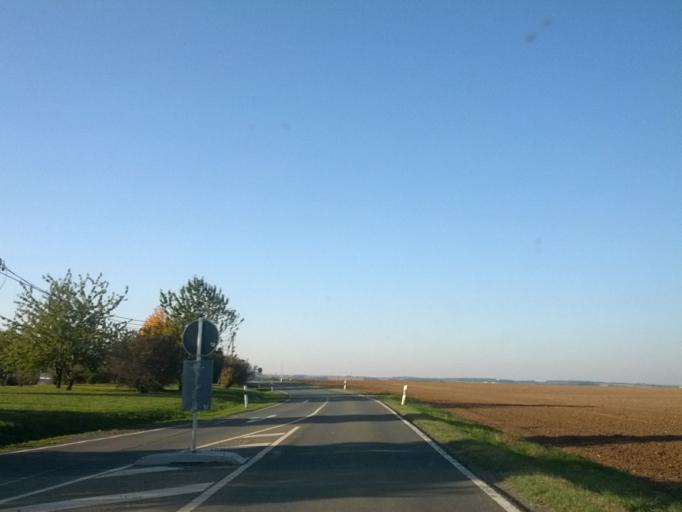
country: DE
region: Thuringia
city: Schwaara
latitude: 50.8863
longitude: 12.1401
